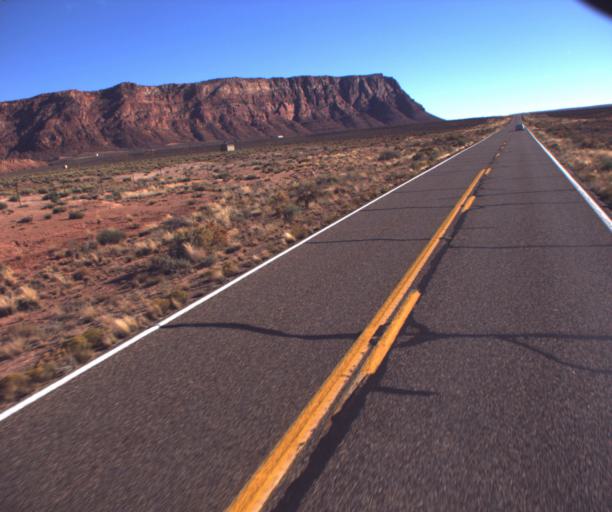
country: US
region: Arizona
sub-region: Coconino County
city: LeChee
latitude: 36.6526
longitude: -111.6509
